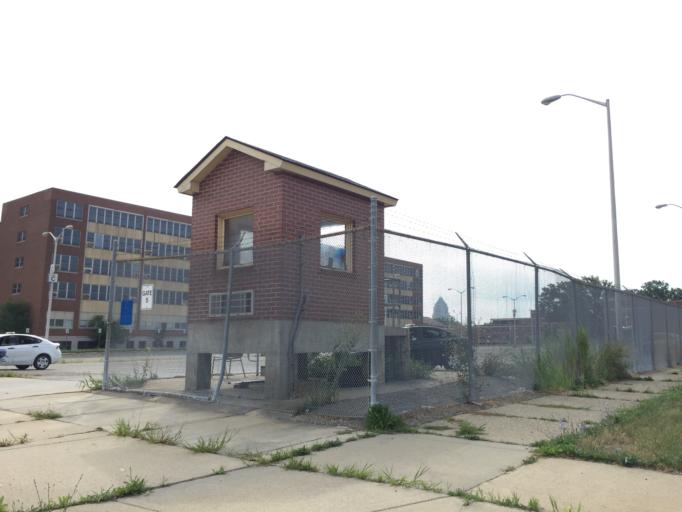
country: US
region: Michigan
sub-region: Wayne County
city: Highland Park
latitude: 42.3777
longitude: -83.0930
